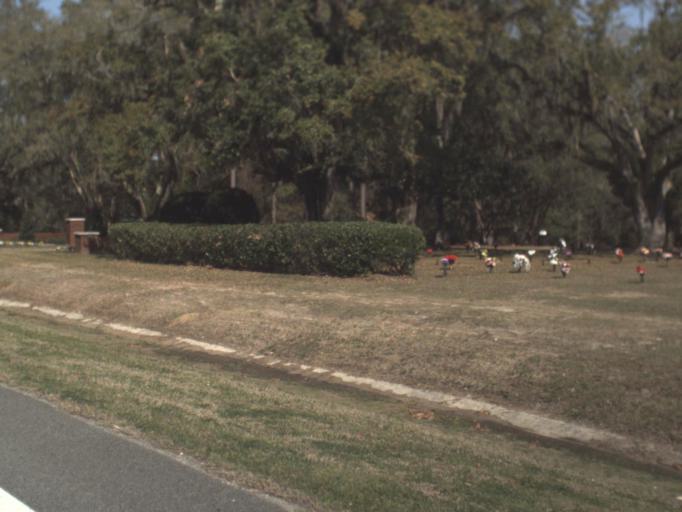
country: US
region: Florida
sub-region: Leon County
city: Tallahassee
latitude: 30.5089
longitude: -84.3386
